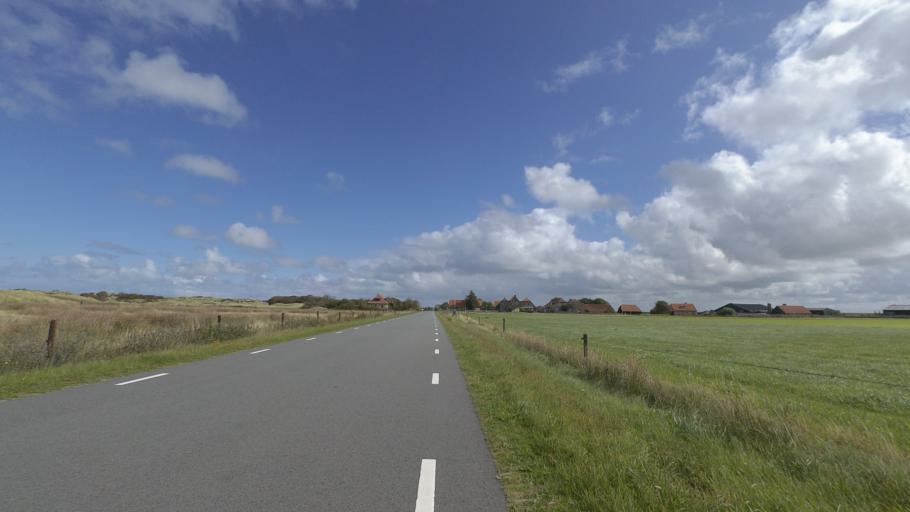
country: NL
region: Friesland
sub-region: Gemeente Ameland
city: Nes
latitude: 53.4499
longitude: 5.8339
